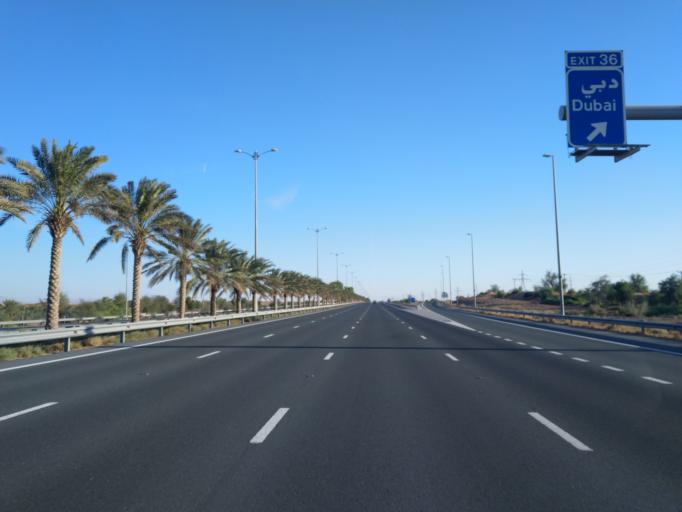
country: OM
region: Al Buraimi
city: Al Buraymi
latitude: 24.5240
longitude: 55.7616
